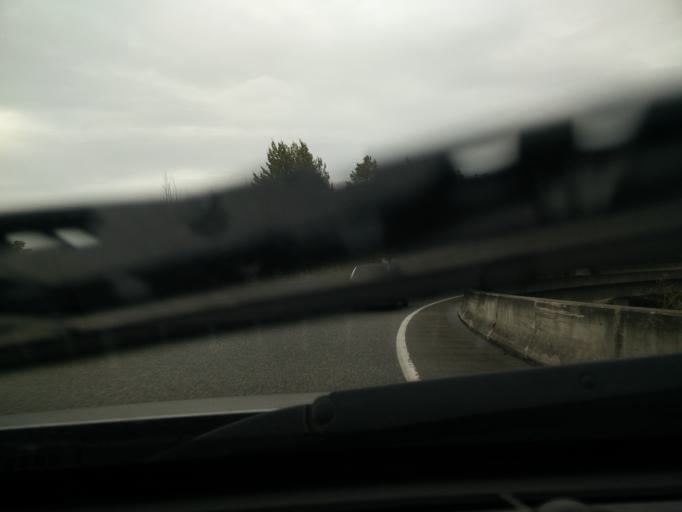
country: US
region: Washington
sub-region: Snohomish County
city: Alderwood Manor
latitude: 47.8339
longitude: -122.2646
